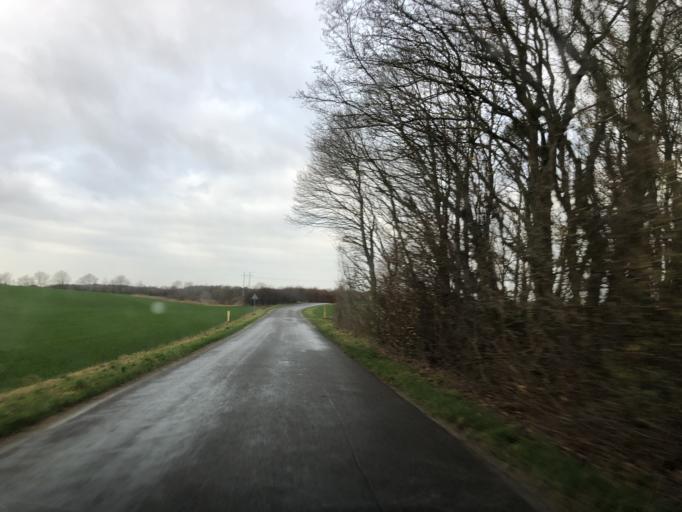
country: DK
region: North Denmark
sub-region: Vesthimmerland Kommune
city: Alestrup
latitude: 56.5937
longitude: 9.6065
